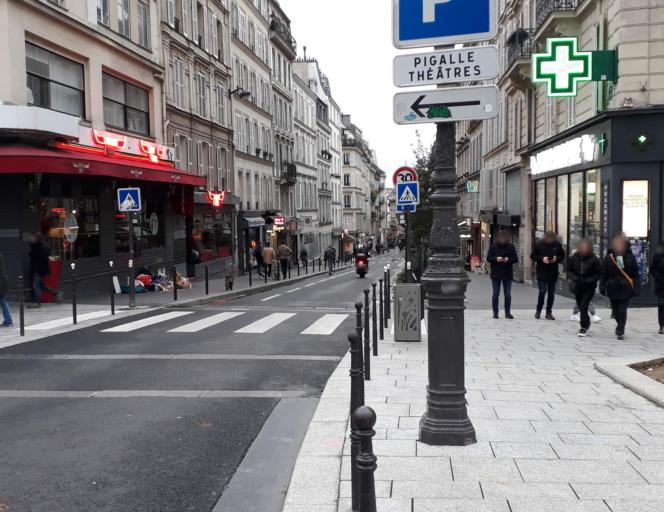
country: FR
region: Ile-de-France
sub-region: Paris
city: Saint-Ouen
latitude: 48.8836
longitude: 2.3324
